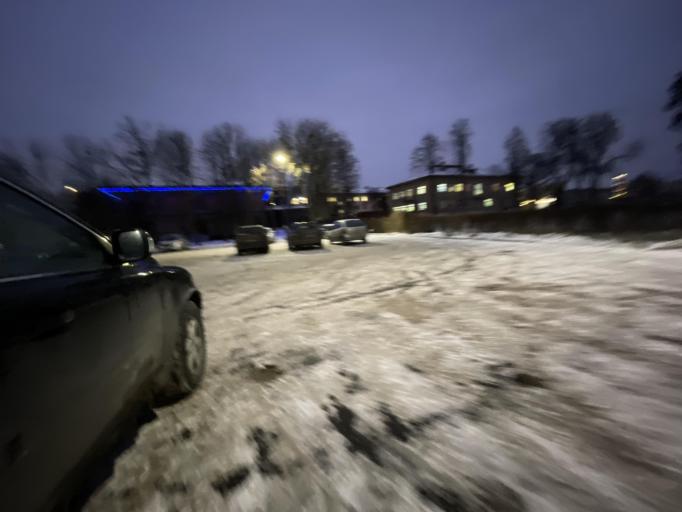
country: BY
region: Grodnenskaya
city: Hrodna
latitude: 53.6813
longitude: 23.8264
